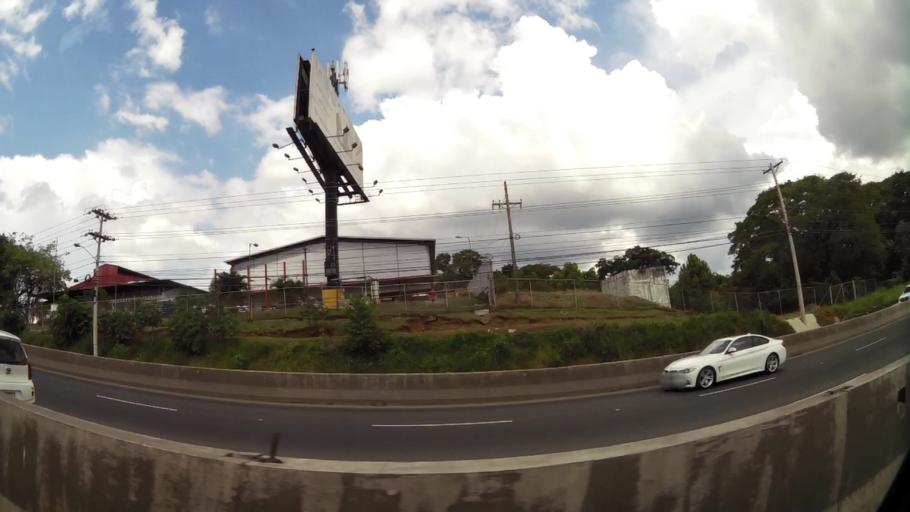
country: PA
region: Panama
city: Tocumen
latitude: 9.0647
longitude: -79.4165
